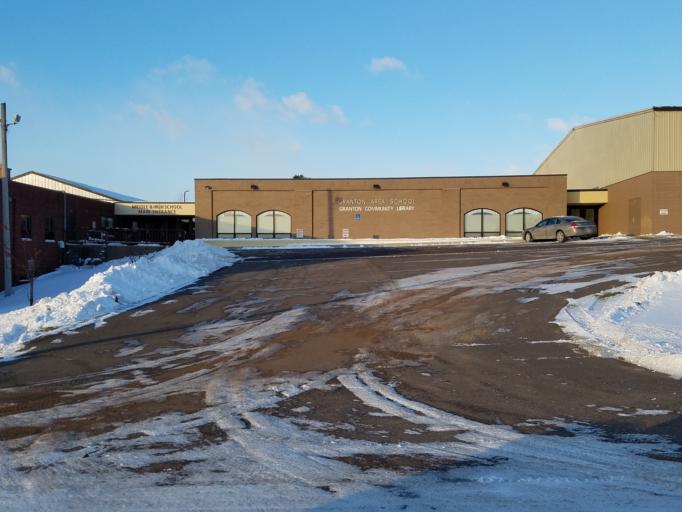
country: US
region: Wisconsin
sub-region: Clark County
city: Neillsville
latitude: 44.5917
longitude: -90.4617
